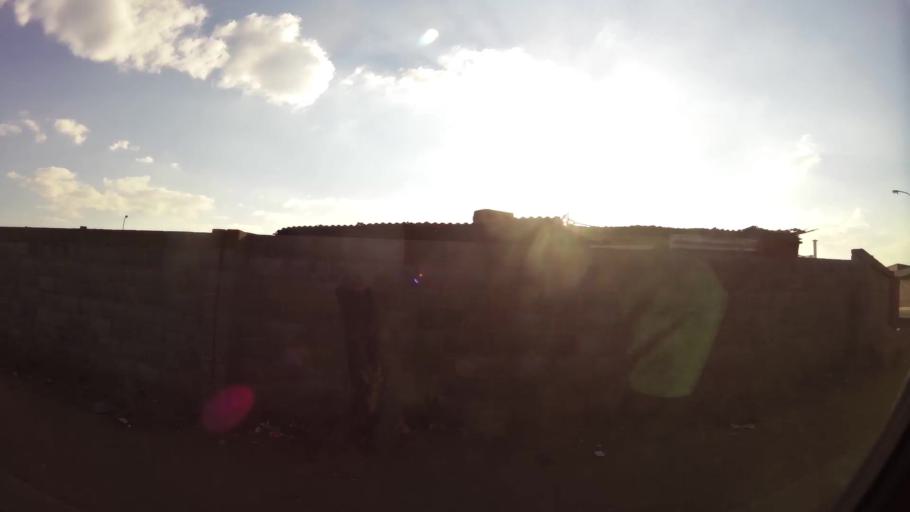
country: ZA
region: Gauteng
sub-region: City of Johannesburg Metropolitan Municipality
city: Soweto
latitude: -26.2268
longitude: 27.8958
